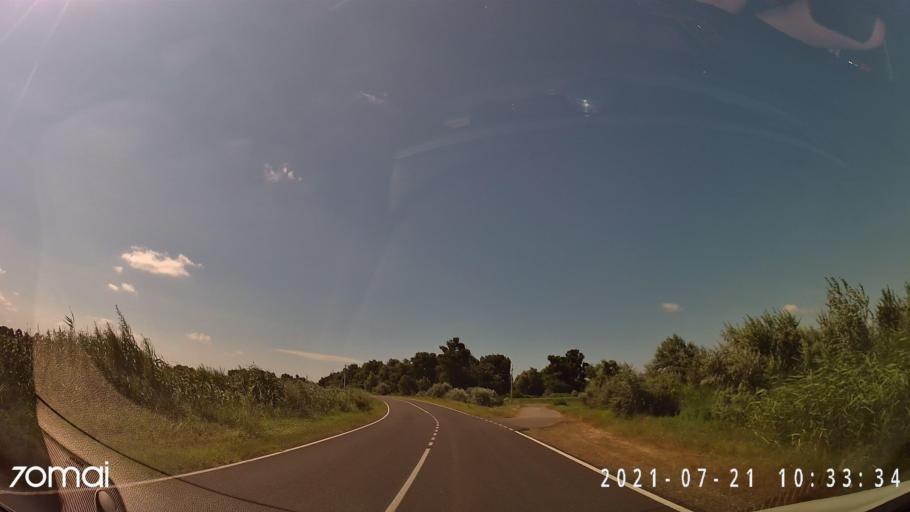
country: RO
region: Tulcea
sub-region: Oras Isaccea
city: Isaccea
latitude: 45.3015
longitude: 28.4368
